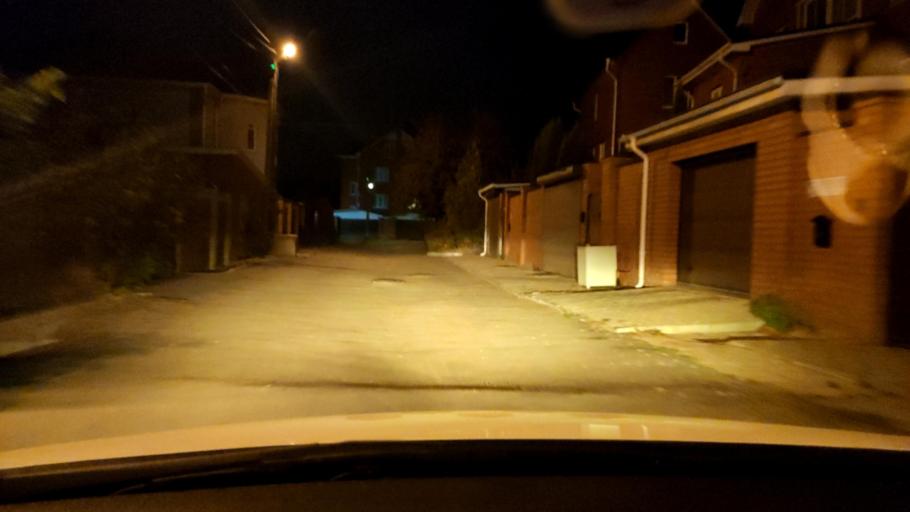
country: RU
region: Voronezj
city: Pridonskoy
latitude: 51.6546
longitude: 39.0892
